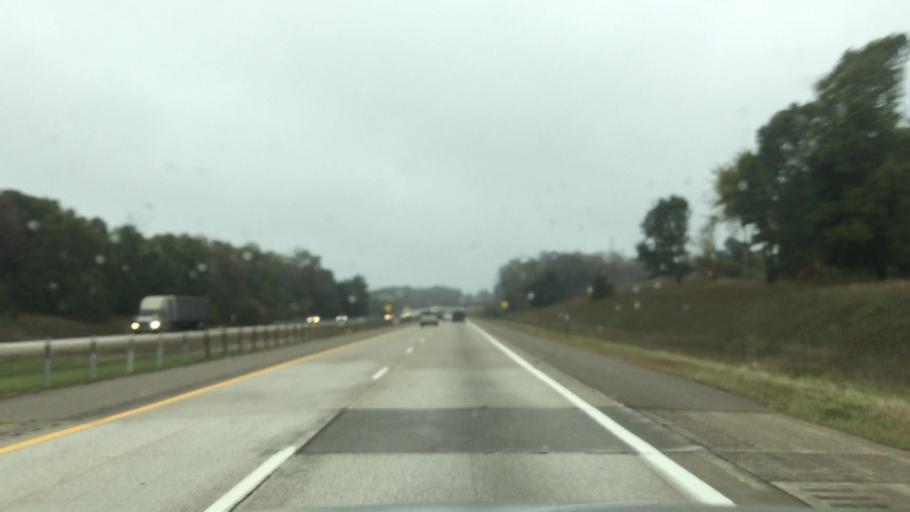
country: US
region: Michigan
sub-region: Van Buren County
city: Paw Paw
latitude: 42.2122
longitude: -85.8678
